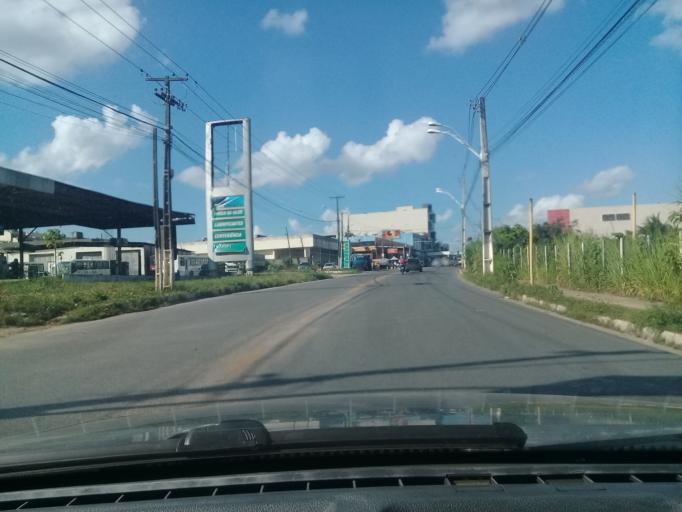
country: BR
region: Pernambuco
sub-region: Vitoria De Santo Antao
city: Vitoria de Santo Antao
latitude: -8.1145
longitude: -35.2953
